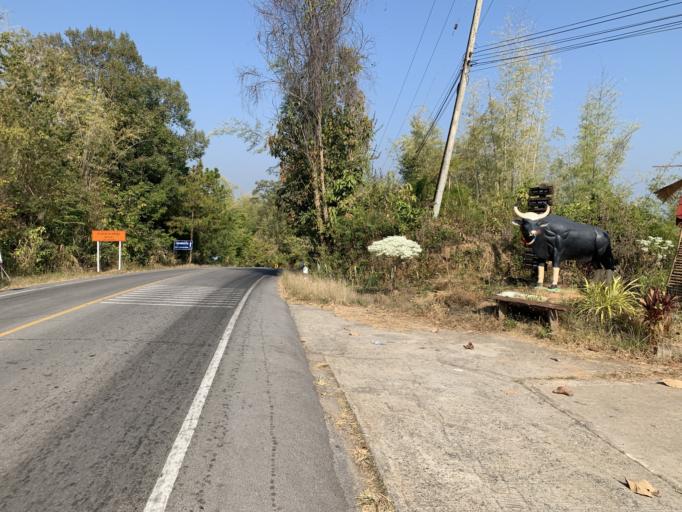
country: TH
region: Loei
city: Loei
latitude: 17.4953
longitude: 101.6040
